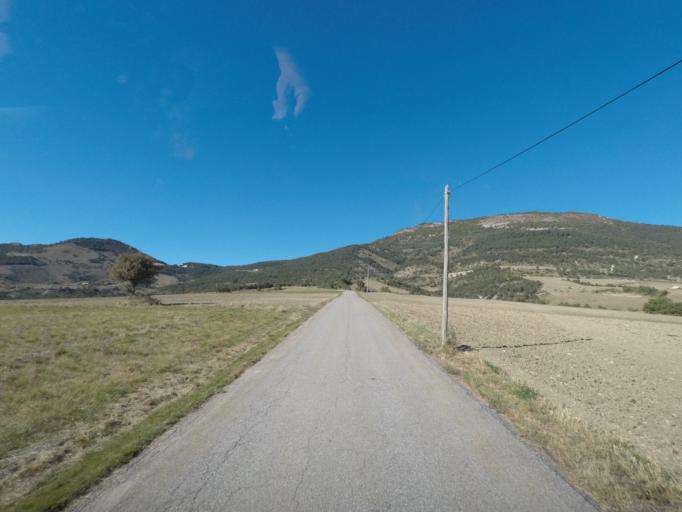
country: FR
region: Provence-Alpes-Cote d'Azur
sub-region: Departement des Hautes-Alpes
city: Serres
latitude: 44.4211
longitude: 5.5829
